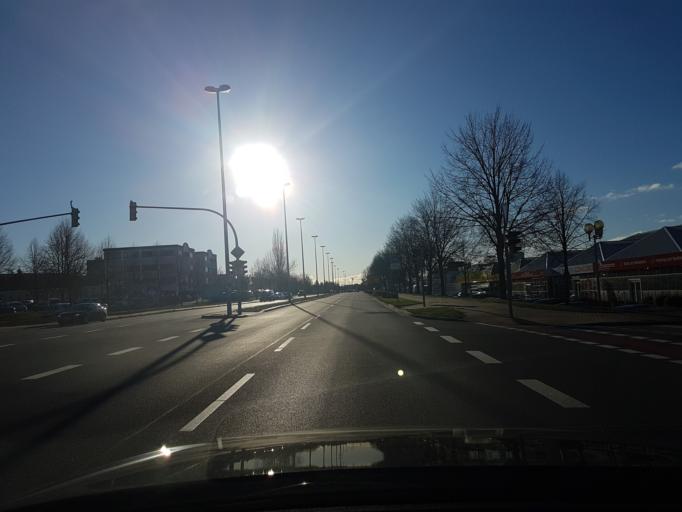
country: DE
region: Mecklenburg-Vorpommern
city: Neubrandenburg
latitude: 53.5824
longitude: 13.2710
